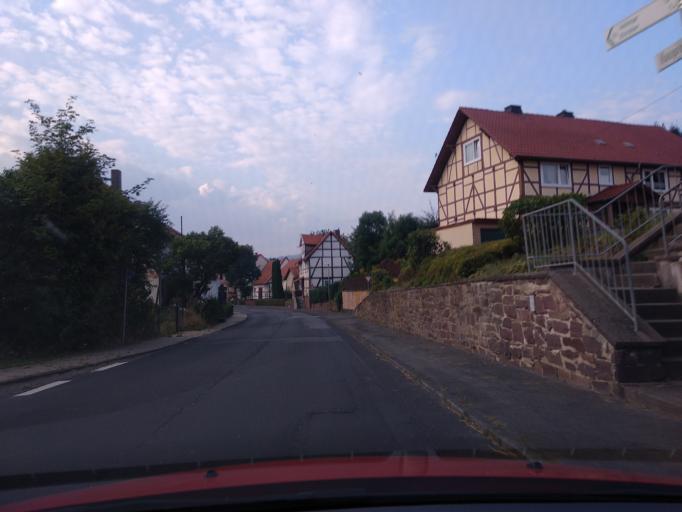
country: DE
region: Hesse
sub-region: Regierungsbezirk Kassel
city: Calden
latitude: 51.4053
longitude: 9.3519
